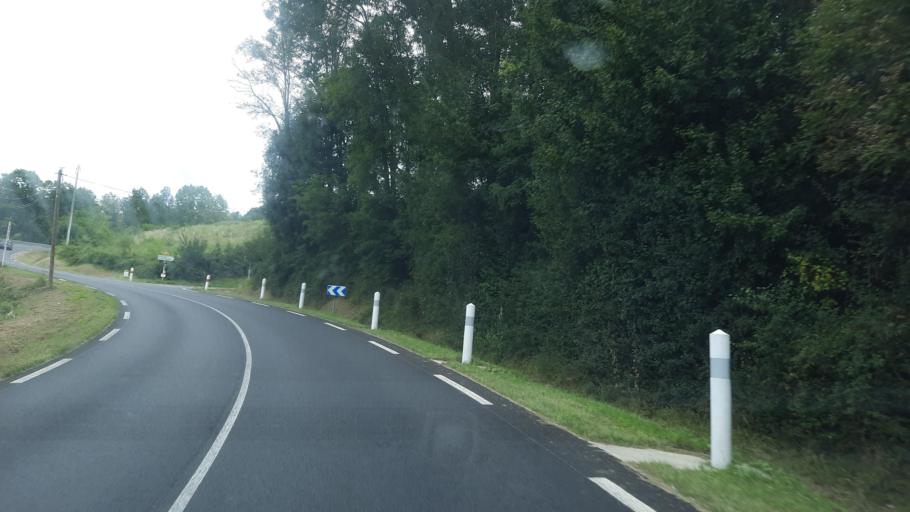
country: FR
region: Midi-Pyrenees
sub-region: Departement des Hautes-Pyrenees
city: Semeac
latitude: 43.2471
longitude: 0.1335
